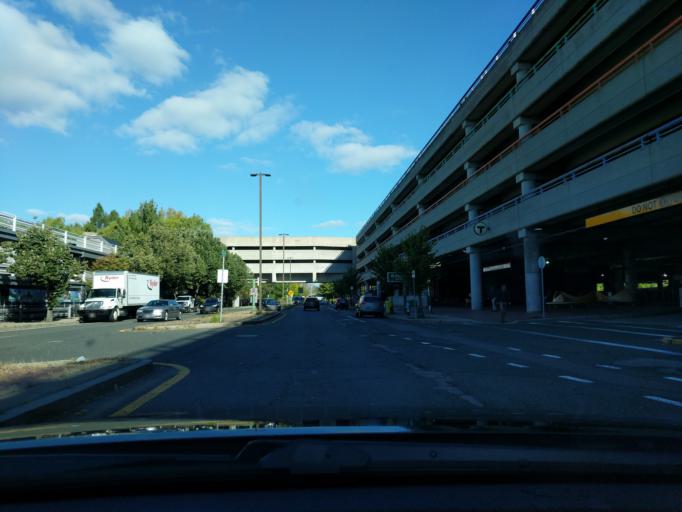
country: US
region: Massachusetts
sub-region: Middlesex County
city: Arlington
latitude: 42.3951
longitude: -71.1425
